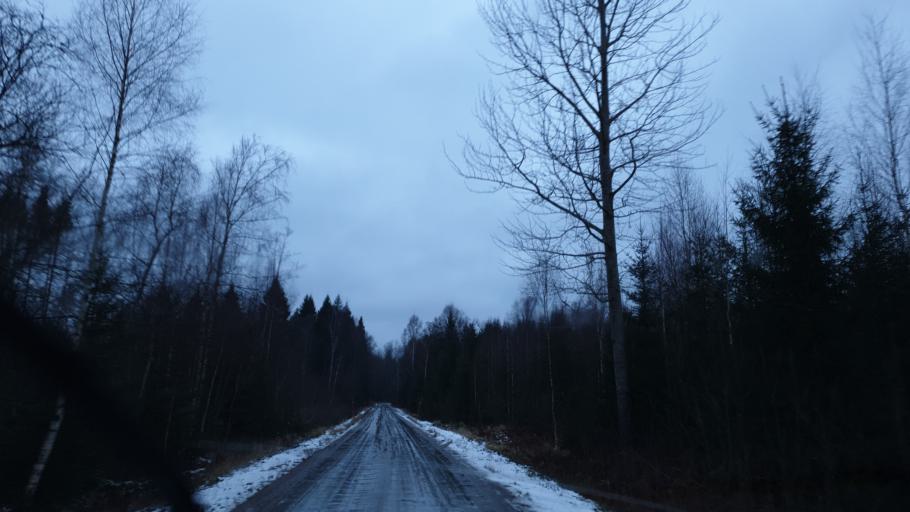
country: SE
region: Uppsala
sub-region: Tierps Kommun
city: Tierp
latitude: 60.3469
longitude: 17.4674
